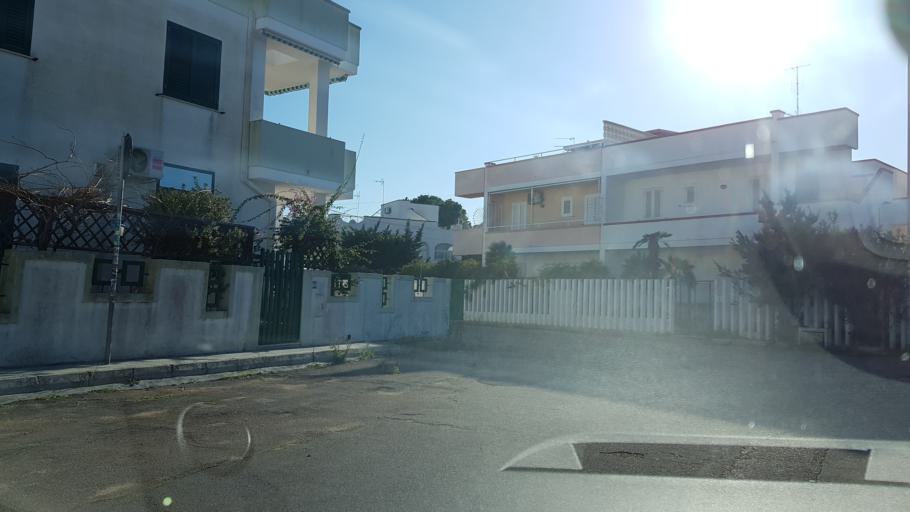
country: IT
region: Apulia
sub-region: Provincia di Lecce
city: Gallipoli
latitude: 40.0363
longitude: 18.0180
